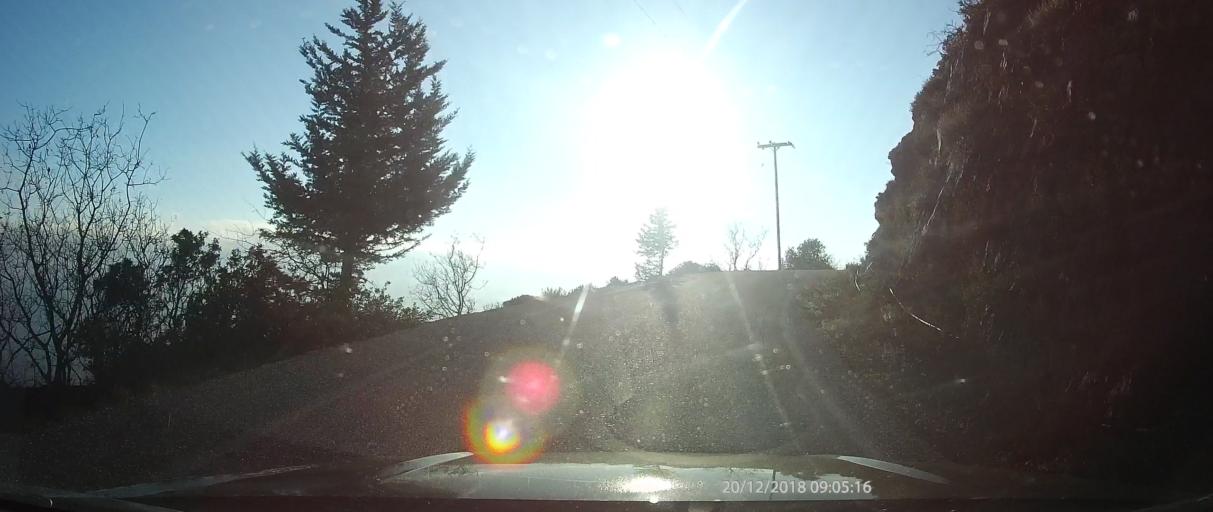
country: GR
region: Peloponnese
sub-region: Nomos Lakonias
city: Sykea
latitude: 36.9421
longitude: 22.9962
